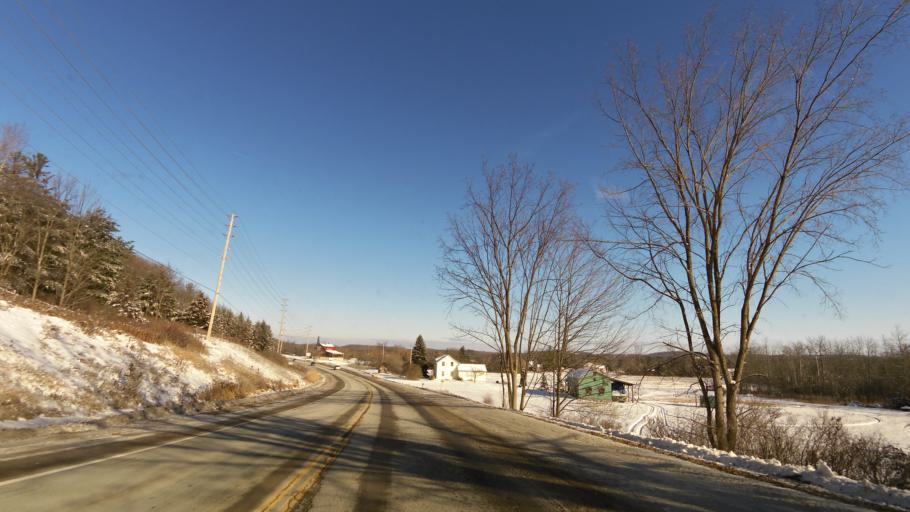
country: CA
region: Ontario
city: Quinte West
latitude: 44.2440
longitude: -77.8170
